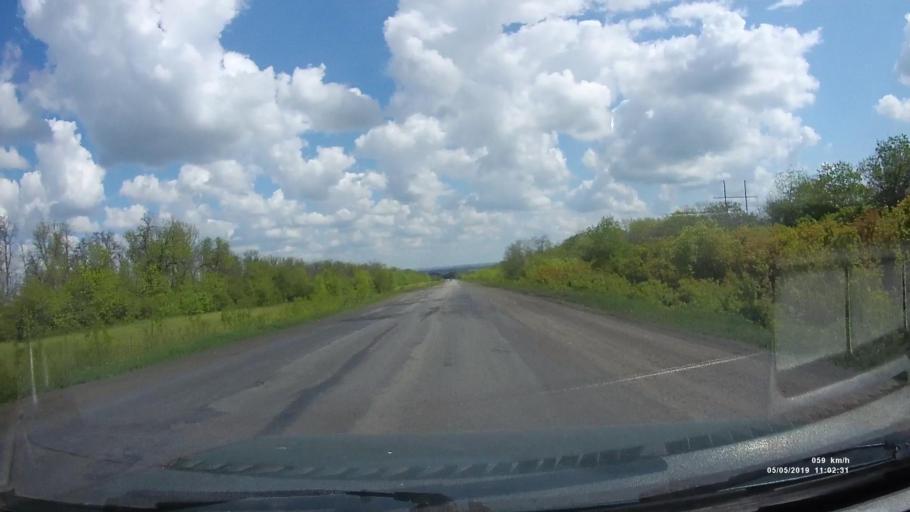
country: RU
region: Rostov
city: Ust'-Donetskiy
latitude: 47.6852
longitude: 40.9093
